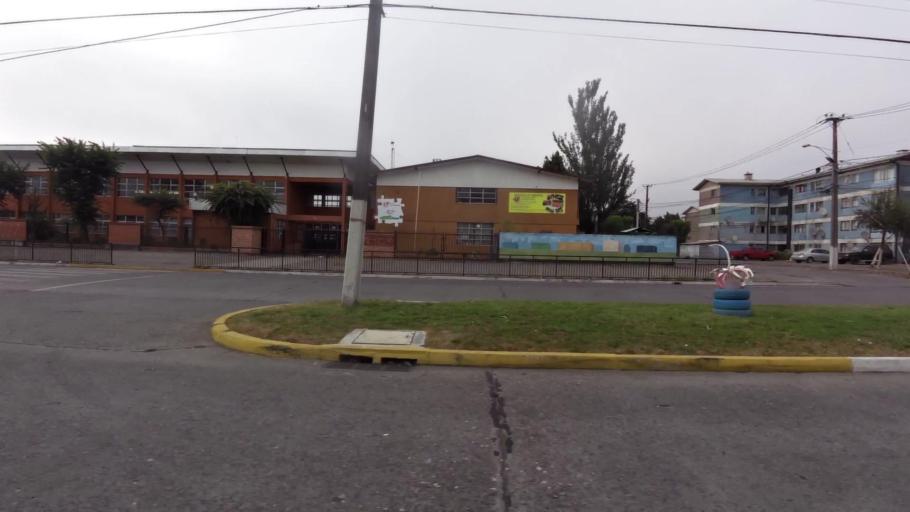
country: CL
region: Biobio
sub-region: Provincia de Concepcion
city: Concepcion
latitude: -36.7912
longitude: -73.0931
